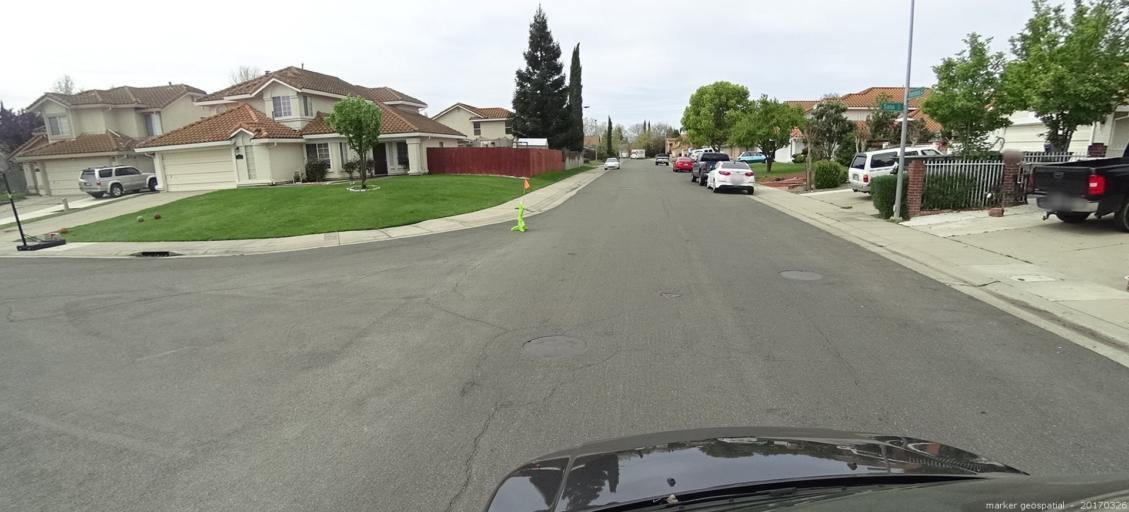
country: US
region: California
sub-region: Sacramento County
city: Laguna
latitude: 38.4422
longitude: -121.4392
